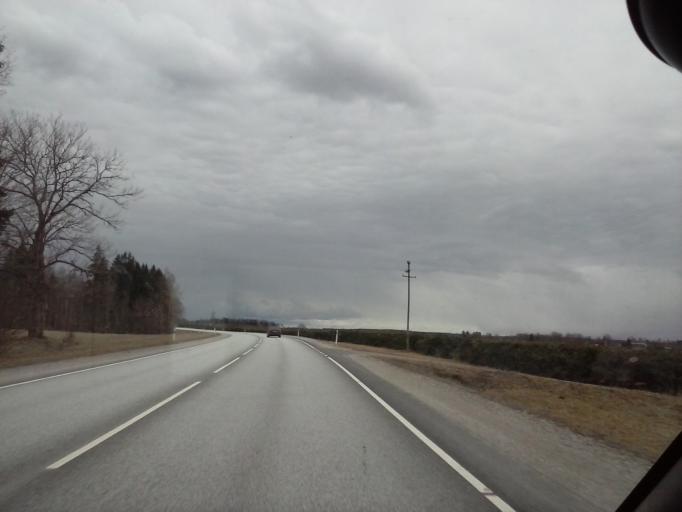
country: EE
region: Jaervamaa
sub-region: Paide linn
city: Paide
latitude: 59.0193
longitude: 25.5847
